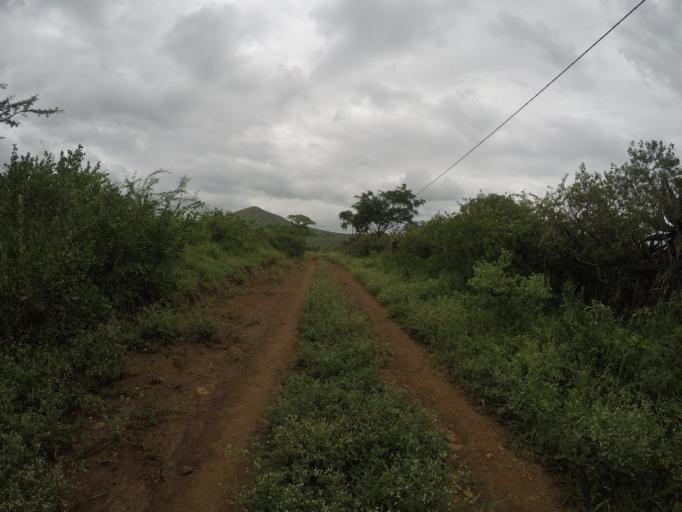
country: ZA
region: KwaZulu-Natal
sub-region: uThungulu District Municipality
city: Empangeni
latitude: -28.5885
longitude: 31.8614
